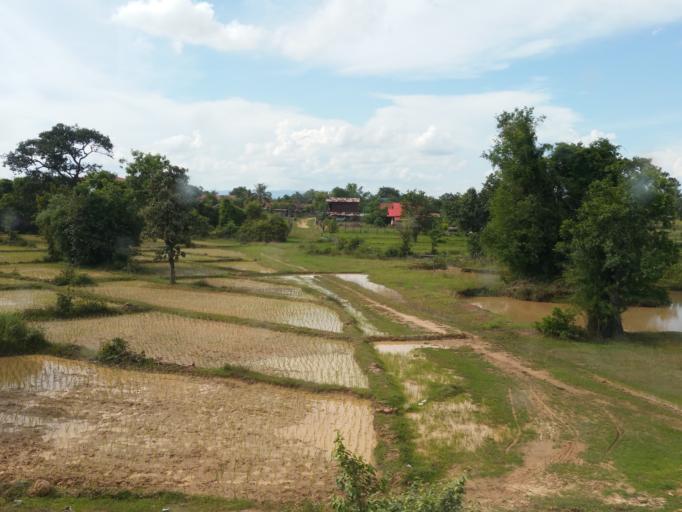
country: LA
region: Champasak
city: Pakxe
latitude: 15.1039
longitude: 105.7636
